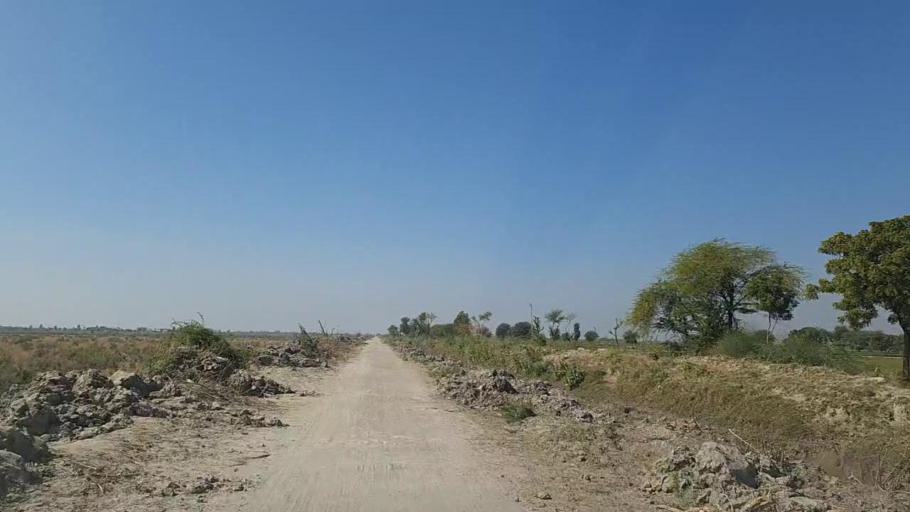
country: PK
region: Sindh
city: Pithoro
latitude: 25.4308
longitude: 69.3612
